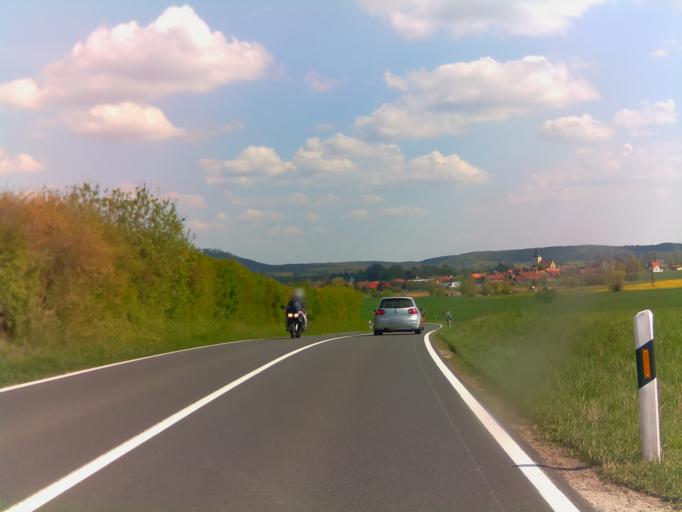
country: DE
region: Thuringia
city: Westhausen
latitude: 50.3633
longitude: 10.6725
